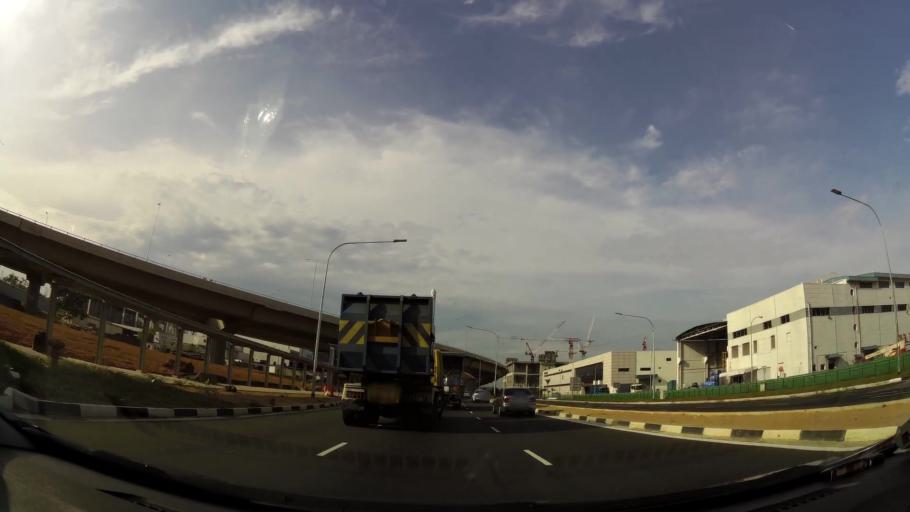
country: MY
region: Johor
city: Johor Bahru
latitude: 1.3301
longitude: 103.6384
